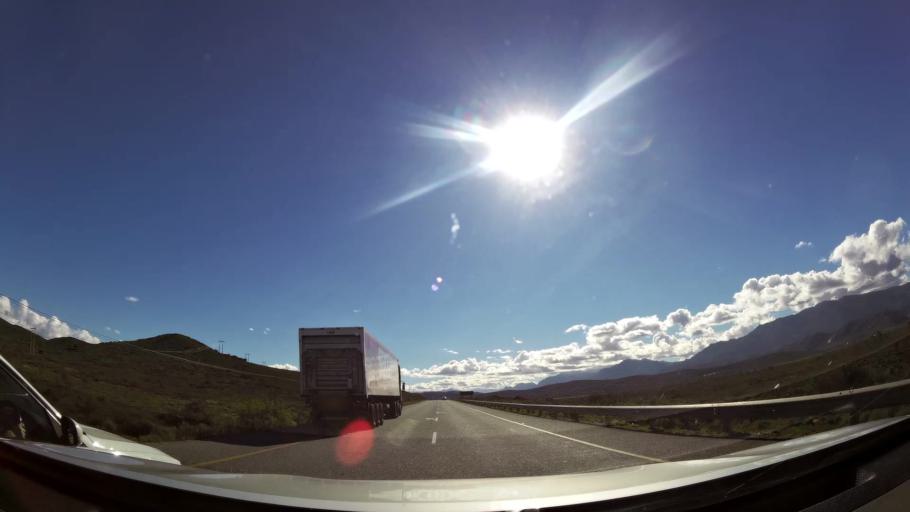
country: ZA
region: Western Cape
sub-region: Cape Winelands District Municipality
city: Worcester
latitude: -33.7608
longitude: 19.7380
